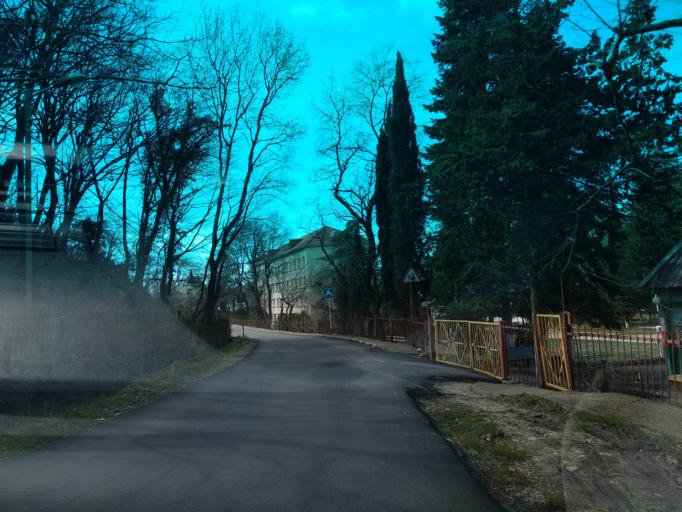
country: RU
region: Krasnodarskiy
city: Shepsi
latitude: 44.0363
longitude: 39.1494
